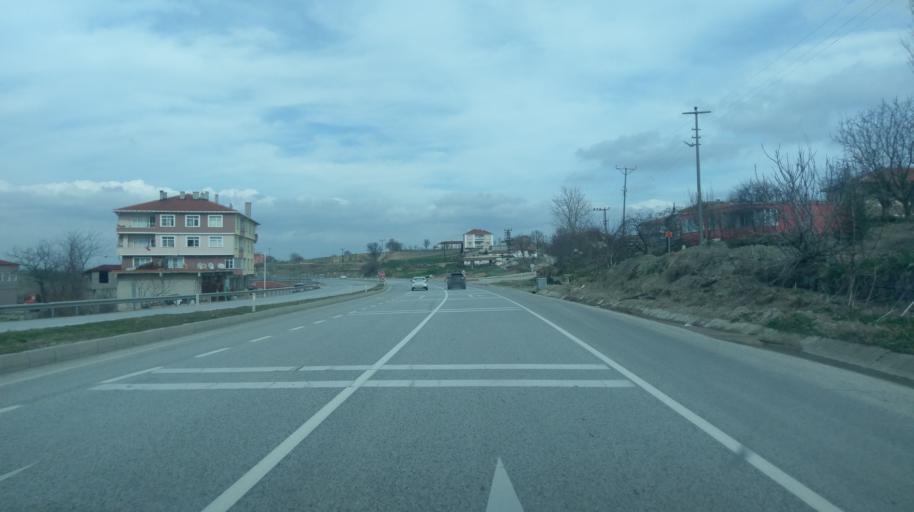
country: TR
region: Edirne
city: Kircasalih
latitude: 41.3956
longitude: 26.8073
